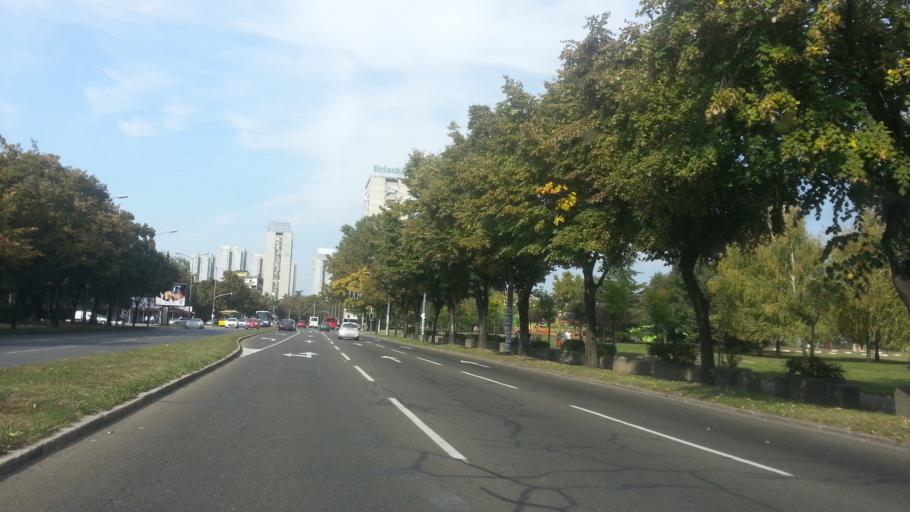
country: RS
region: Central Serbia
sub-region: Belgrade
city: Zemun
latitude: 44.8331
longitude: 20.4186
